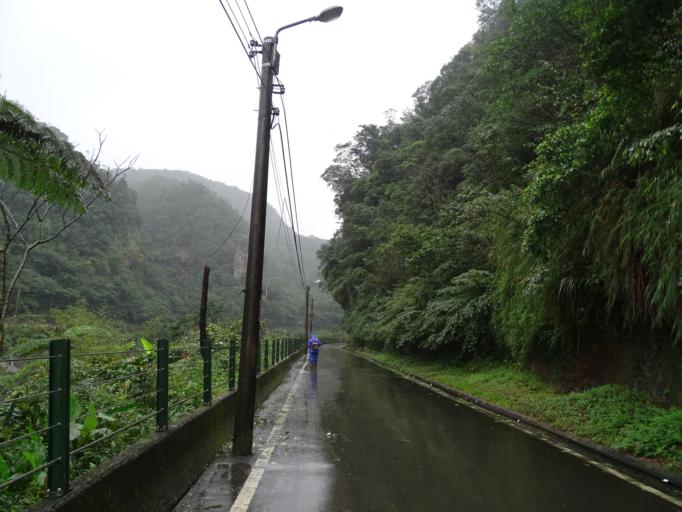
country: TW
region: Taiwan
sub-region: Keelung
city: Keelung
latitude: 25.0673
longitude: 121.8228
